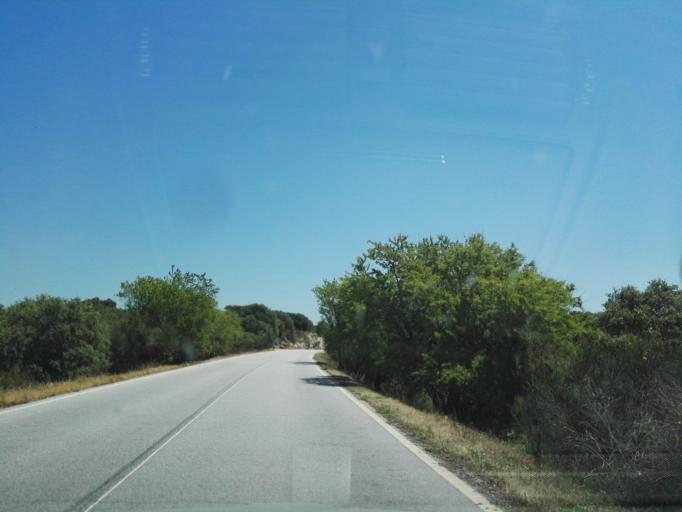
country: PT
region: Portalegre
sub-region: Elvas
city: Elvas
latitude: 39.0014
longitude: -7.2147
